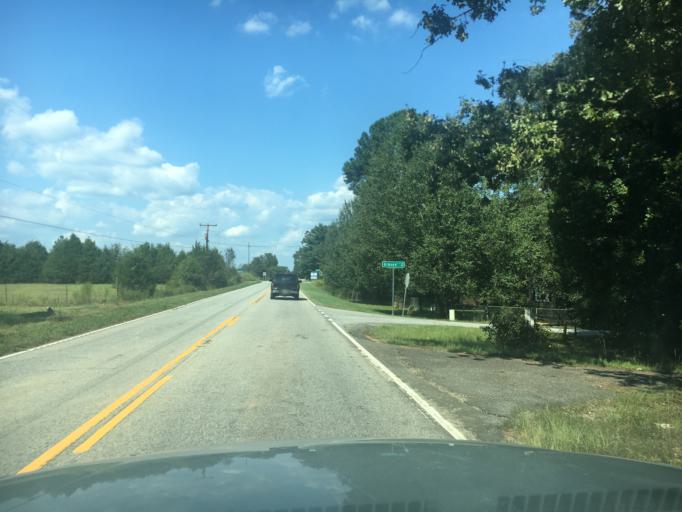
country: US
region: South Carolina
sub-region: Anderson County
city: Pendleton
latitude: 34.6005
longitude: -82.7941
